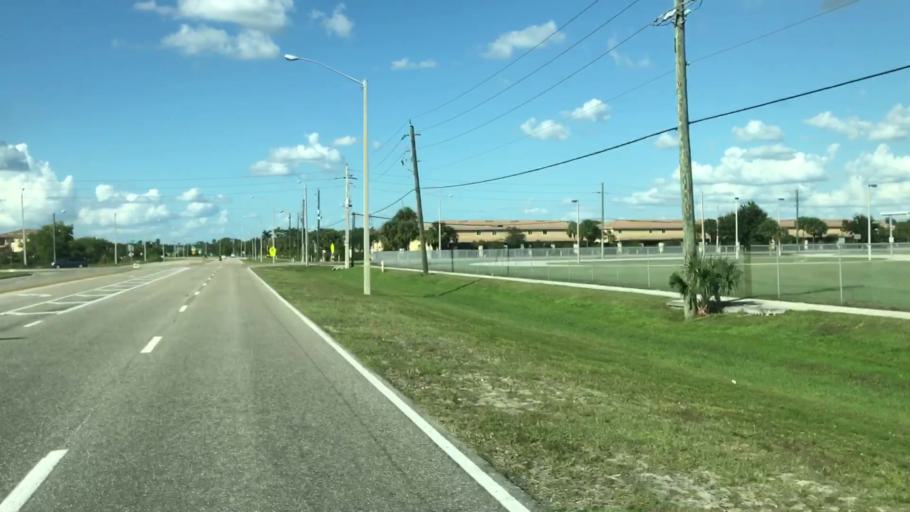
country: US
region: Florida
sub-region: Lee County
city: Fort Myers
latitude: 26.6023
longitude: -81.8182
